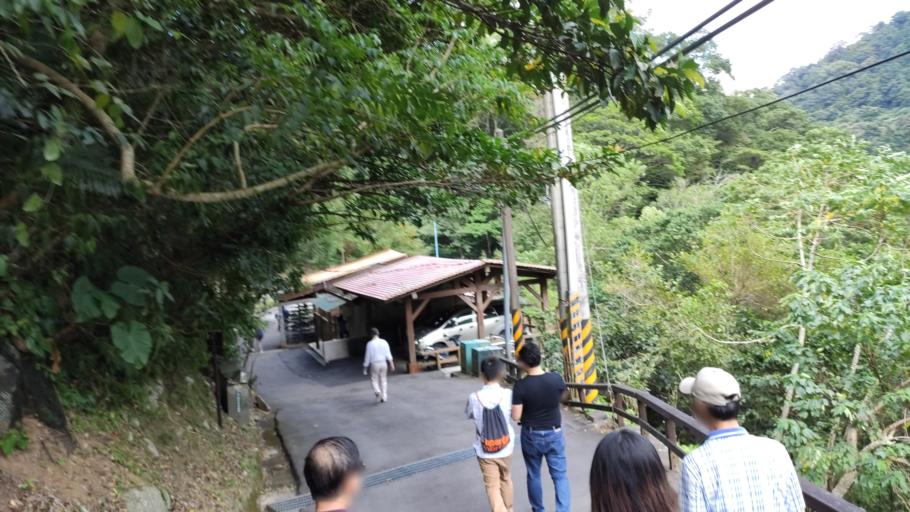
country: TW
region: Taiwan
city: Daxi
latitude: 24.8303
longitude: 121.4447
